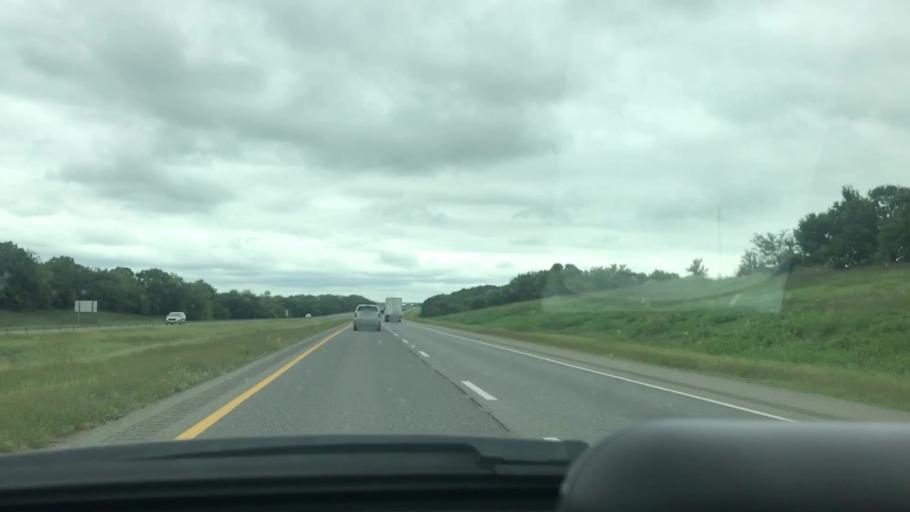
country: US
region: Oklahoma
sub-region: McIntosh County
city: Checotah
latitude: 35.3920
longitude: -95.5653
